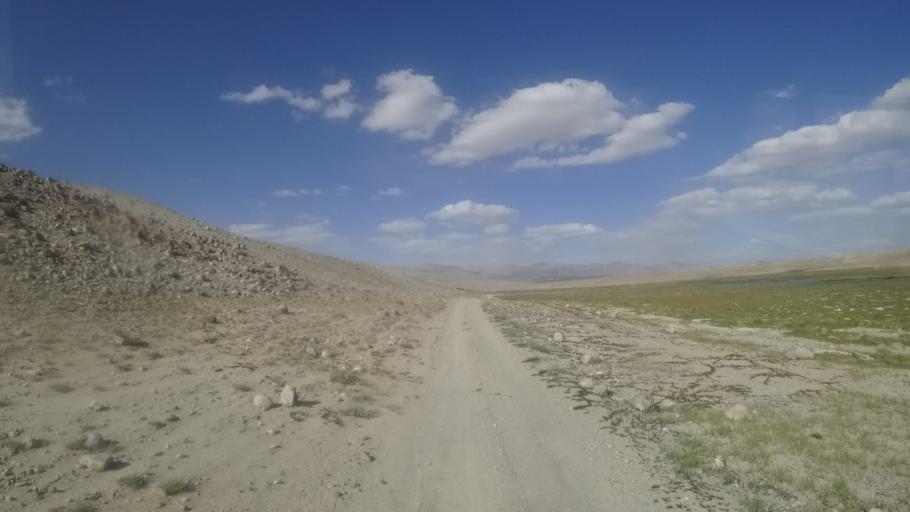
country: AF
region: Badakhshan
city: Khandud
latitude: 37.4126
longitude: 73.2238
